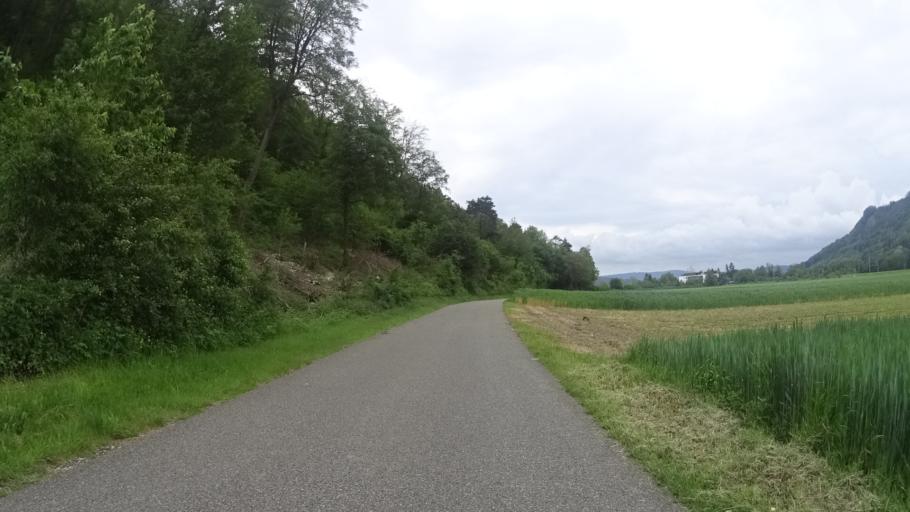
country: CH
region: Aargau
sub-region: Bezirk Brugg
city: Lauffohr (Brugg)
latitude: 47.5105
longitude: 8.2411
